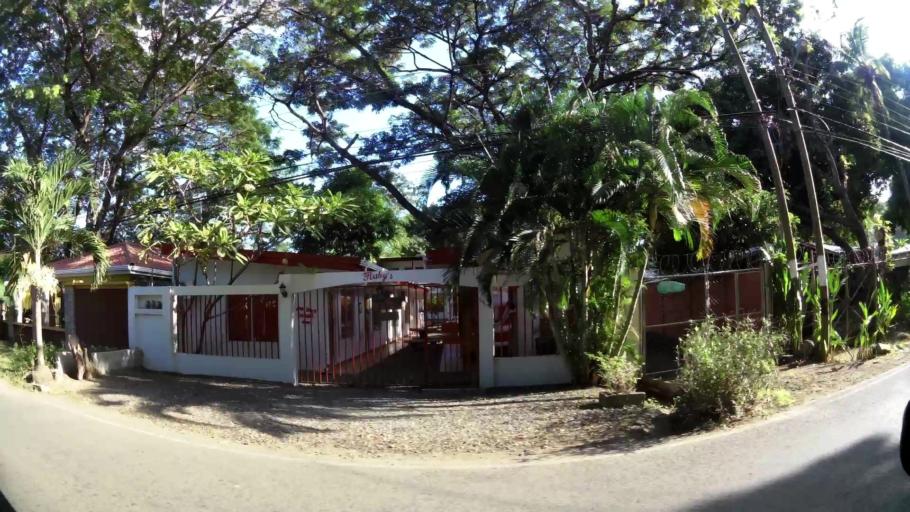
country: CR
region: Guanacaste
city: Sardinal
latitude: 10.5515
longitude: -85.6951
